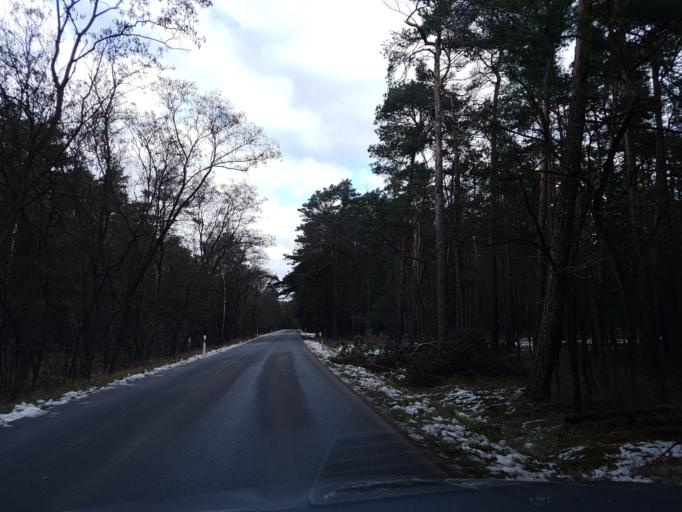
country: DE
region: Brandenburg
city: Merzdorf
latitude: 51.3924
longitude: 13.5230
